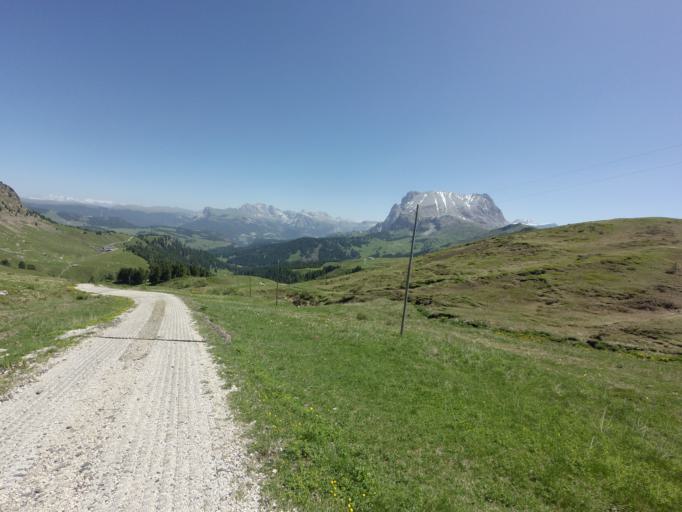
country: IT
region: Trentino-Alto Adige
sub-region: Provincia di Trento
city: Mazzin
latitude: 46.4984
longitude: 11.6494
